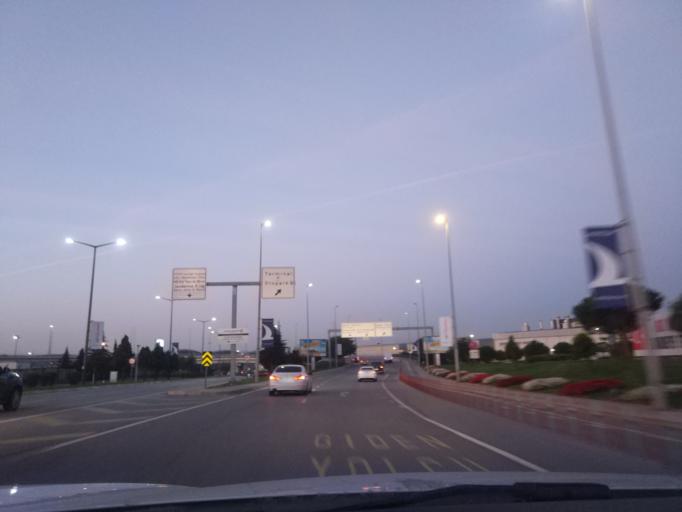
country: TR
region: Istanbul
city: Pendik
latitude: 40.9096
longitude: 29.3126
